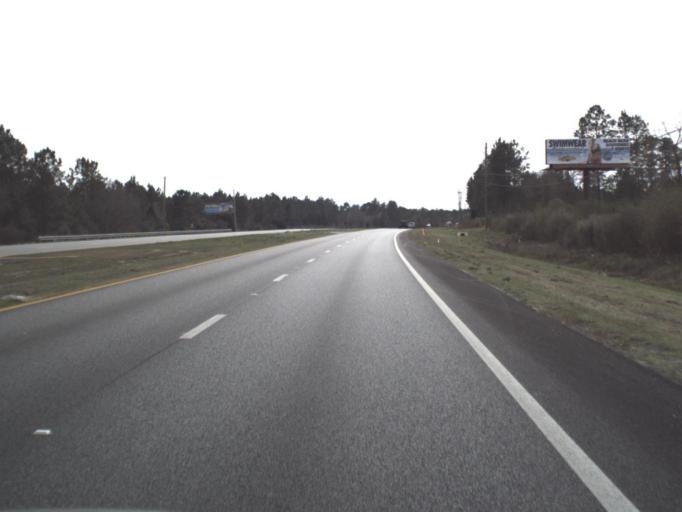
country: US
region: Florida
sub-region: Bay County
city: Youngstown
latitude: 30.3331
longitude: -85.4443
